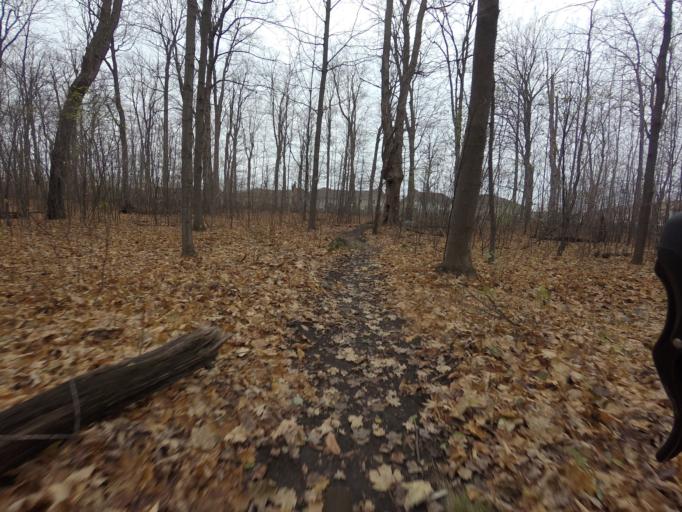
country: CA
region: Ontario
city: Bells Corners
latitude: 45.2723
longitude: -75.7134
